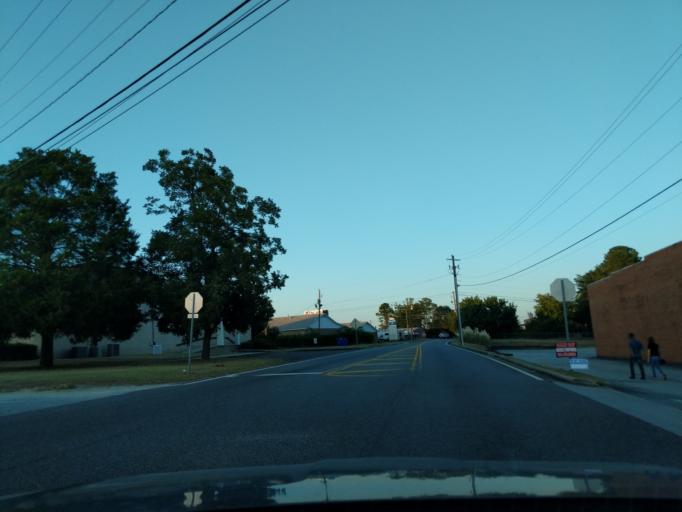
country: US
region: Georgia
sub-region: Columbia County
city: Martinez
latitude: 33.5091
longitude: -82.0926
